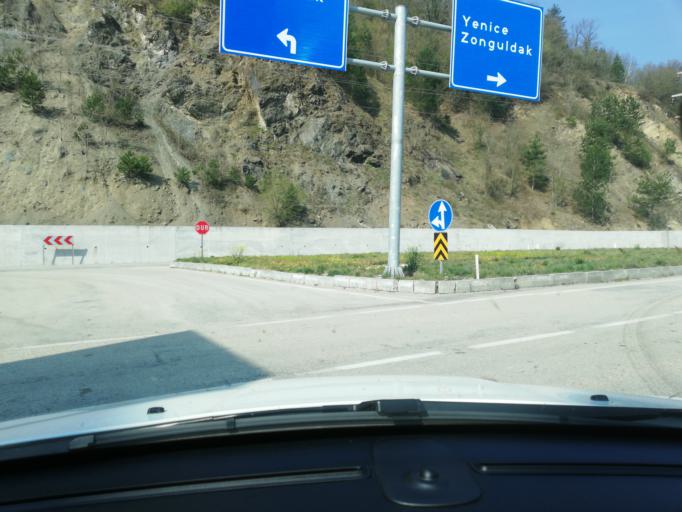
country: TR
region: Karabuk
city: Yenice
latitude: 41.2061
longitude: 32.3655
